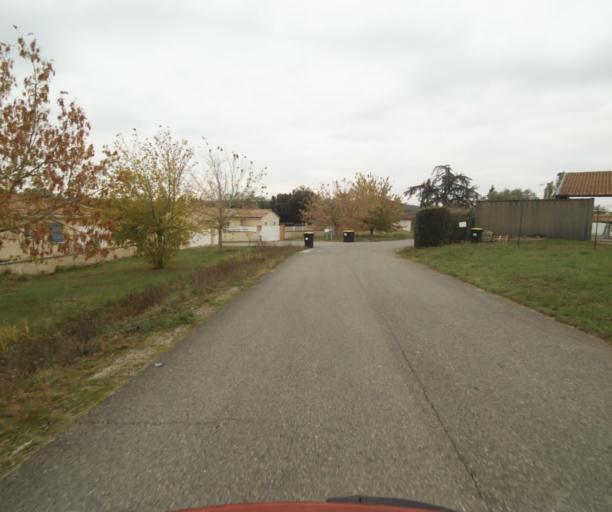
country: FR
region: Midi-Pyrenees
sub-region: Departement du Tarn-et-Garonne
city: Verdun-sur-Garonne
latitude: 43.8004
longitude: 1.2211
